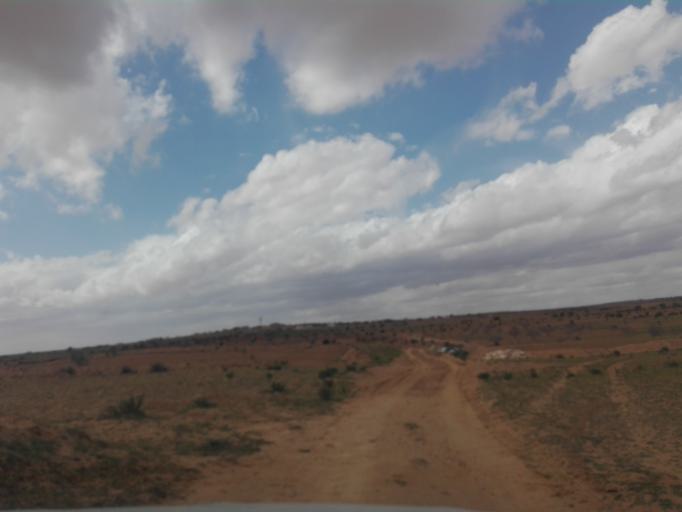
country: TN
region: Safaqis
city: Sfax
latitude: 34.6980
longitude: 10.4431
